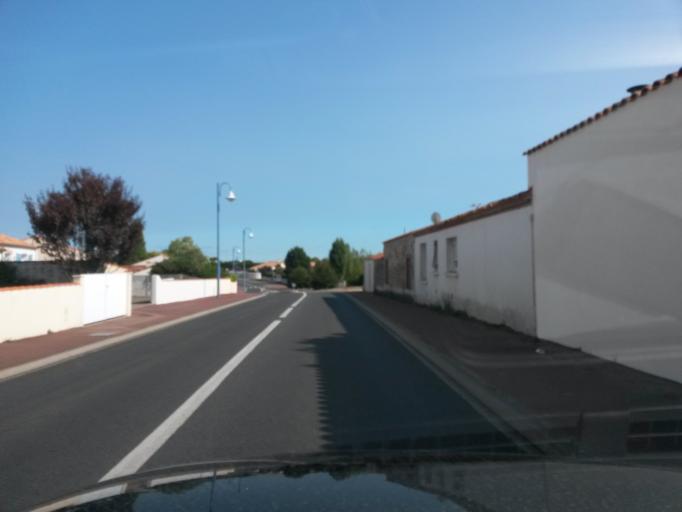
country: FR
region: Pays de la Loire
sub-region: Departement de la Vendee
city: Bretignolles-sur-Mer
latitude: 46.6019
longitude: -1.8271
